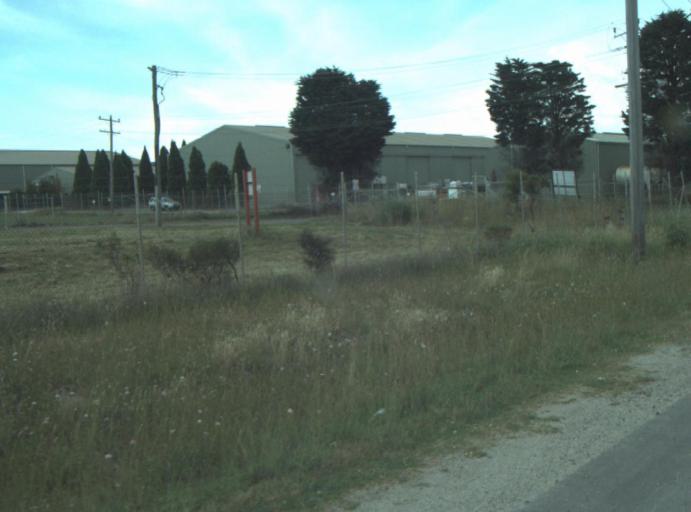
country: AU
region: Victoria
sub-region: Greater Geelong
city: Leopold
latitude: -38.1621
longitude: 144.4285
